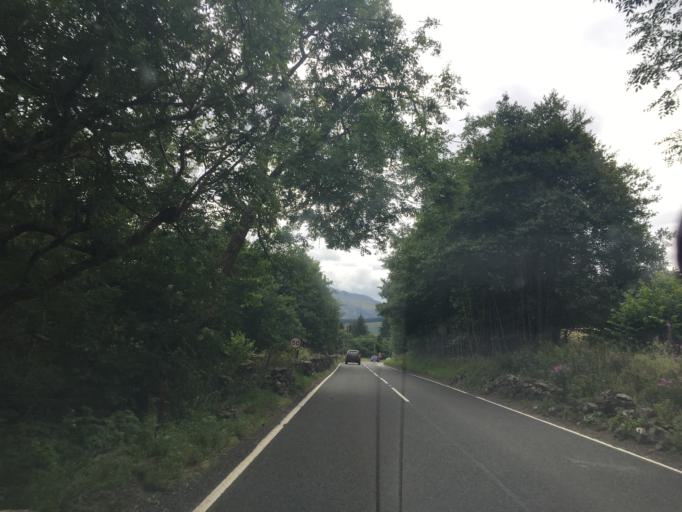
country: GB
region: Scotland
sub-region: Stirling
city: Callander
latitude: 56.3956
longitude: -4.2951
